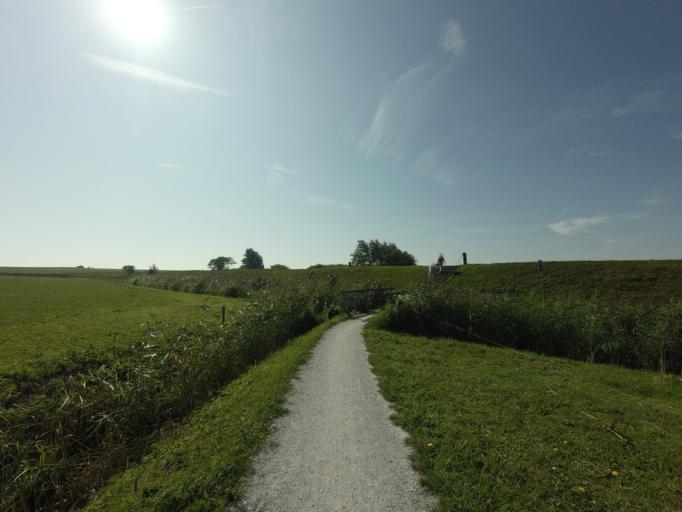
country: NL
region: Friesland
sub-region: Gemeente Schiermonnikoog
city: Schiermonnikoog
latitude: 53.4734
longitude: 6.1552
